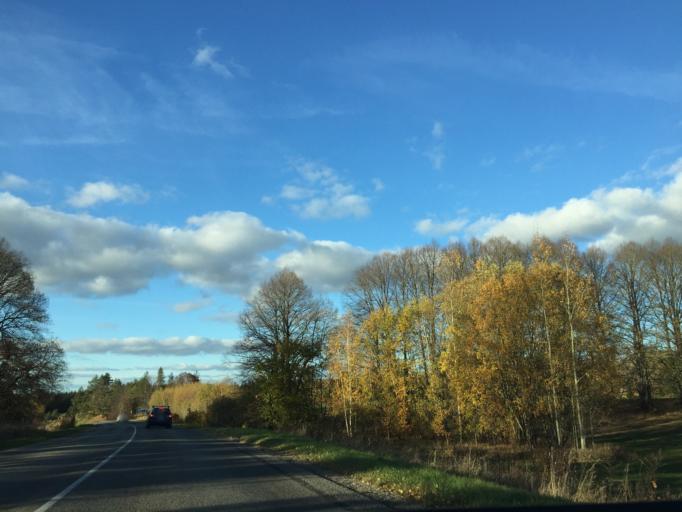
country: LV
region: Tukuma Rajons
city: Tukums
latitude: 56.9998
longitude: 23.0849
